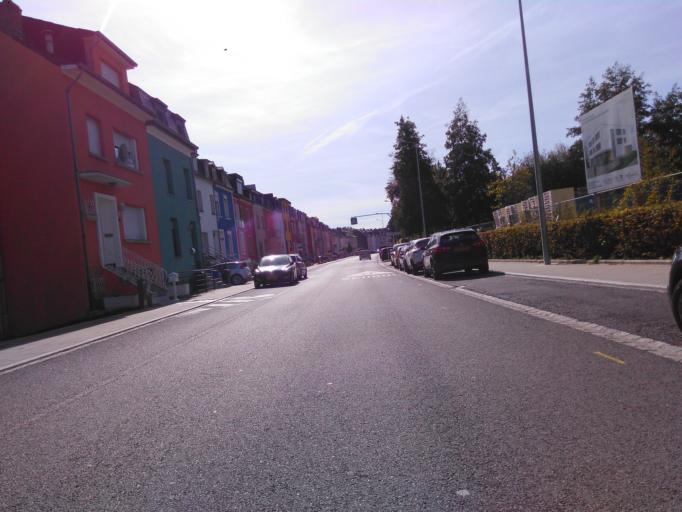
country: LU
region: Luxembourg
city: Tetange
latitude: 49.4814
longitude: 6.0372
